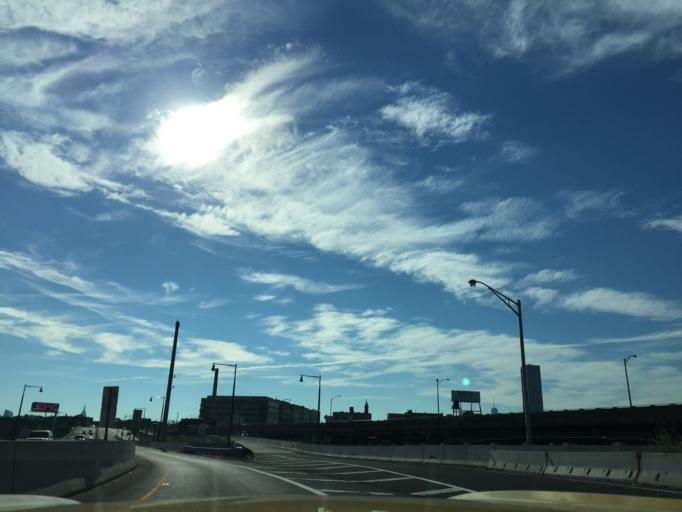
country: US
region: New Jersey
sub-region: Hudson County
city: Jersey City
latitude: 40.7391
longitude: -74.0751
